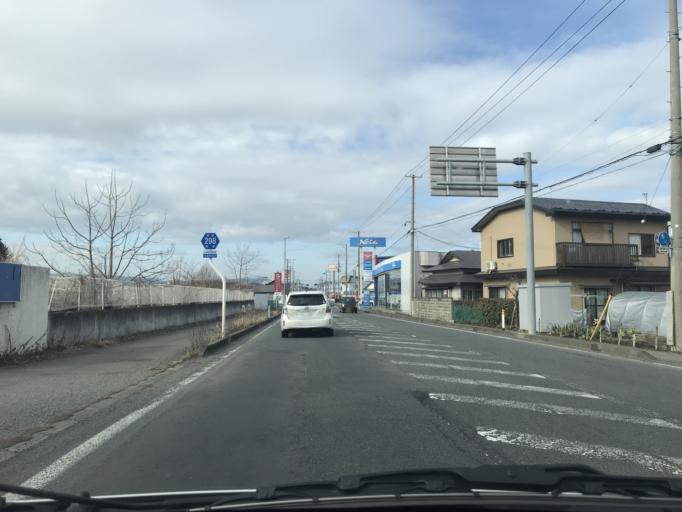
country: JP
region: Iwate
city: Hanamaki
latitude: 39.3877
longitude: 141.1249
